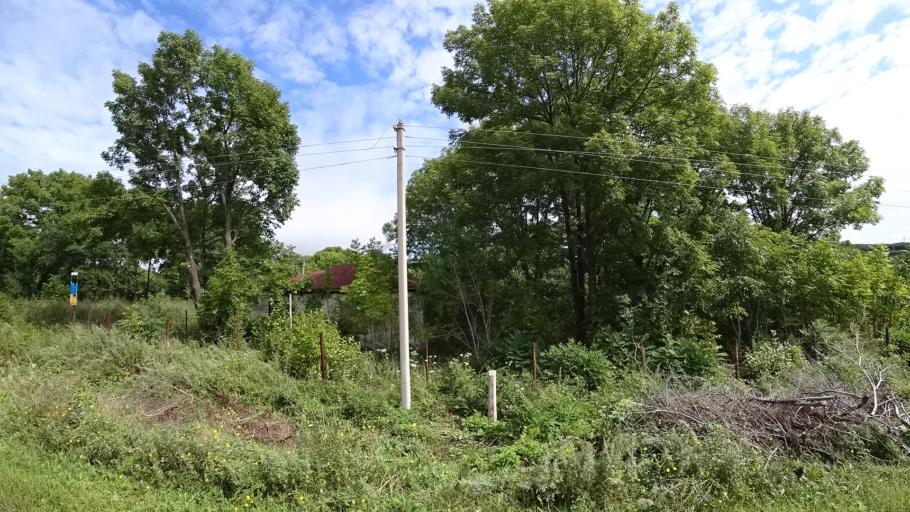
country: RU
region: Primorskiy
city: Lyalichi
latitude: 44.1377
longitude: 132.3878
